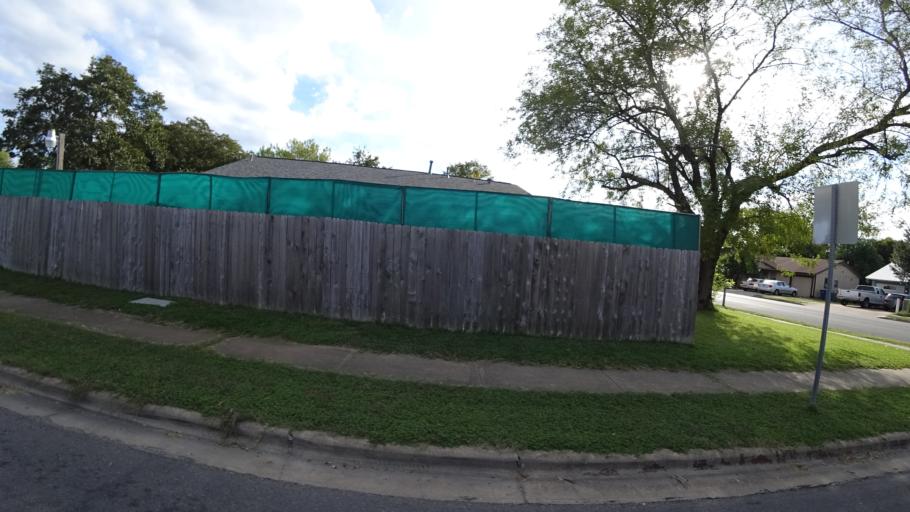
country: US
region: Texas
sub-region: Travis County
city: Onion Creek
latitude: 30.1930
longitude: -97.7571
